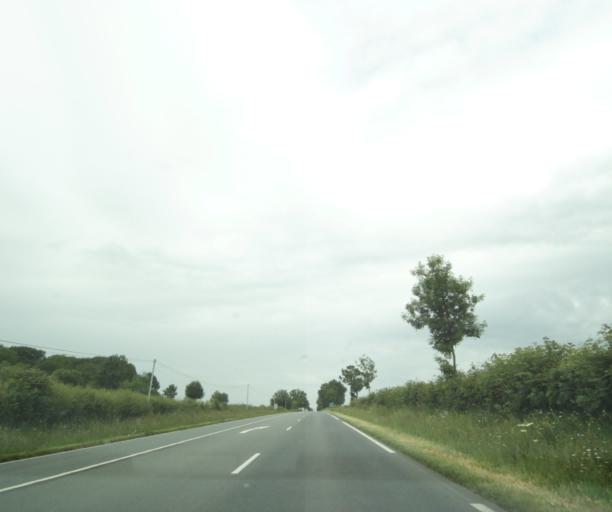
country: FR
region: Poitou-Charentes
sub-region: Departement des Deux-Sevres
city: Saint-Pardoux
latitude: 46.5955
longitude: -0.2897
